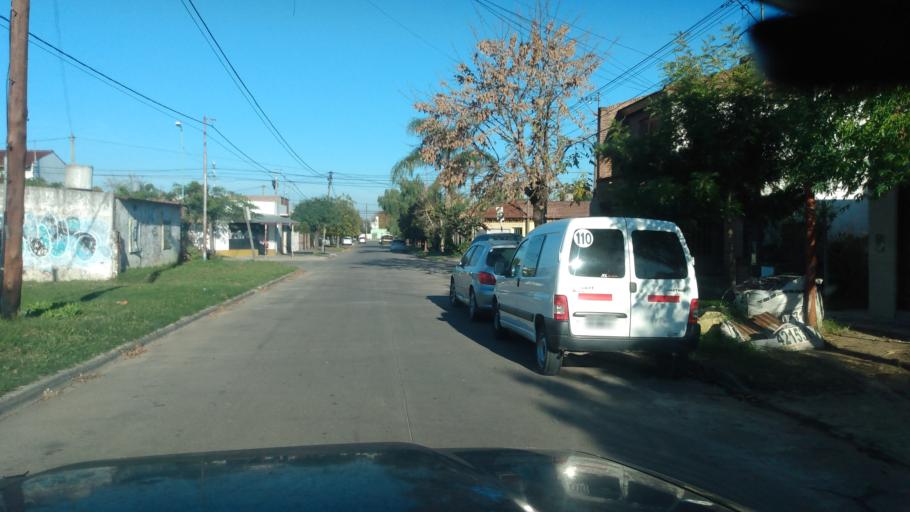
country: AR
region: Buenos Aires
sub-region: Partido de Lujan
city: Lujan
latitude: -34.5607
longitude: -59.0976
